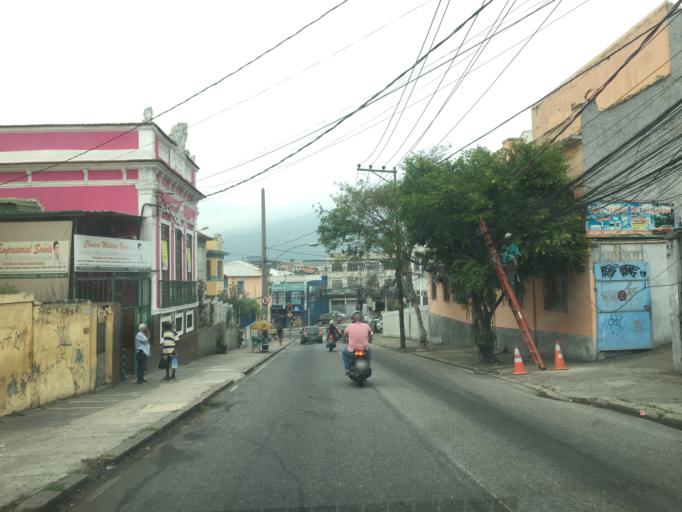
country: BR
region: Rio de Janeiro
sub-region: Rio De Janeiro
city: Rio de Janeiro
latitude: -22.8988
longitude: -43.2277
